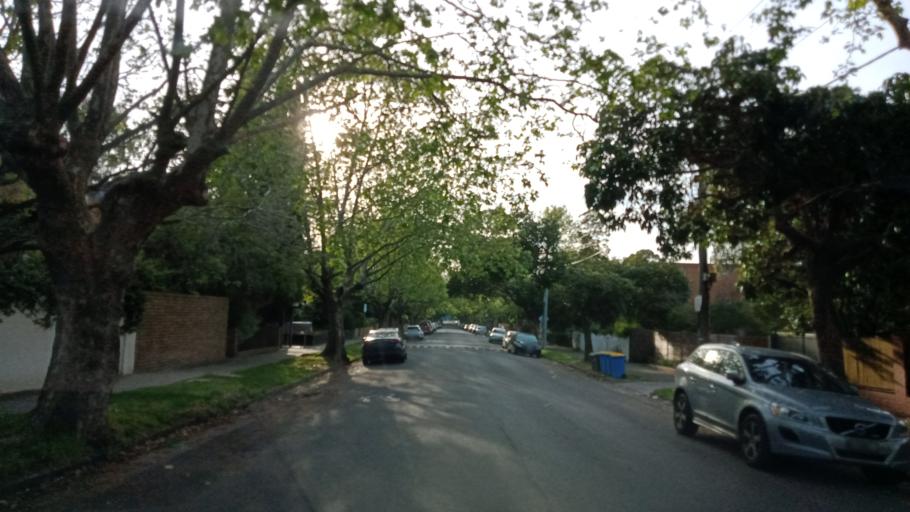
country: AU
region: Victoria
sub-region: Boroondara
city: Hawthorn East
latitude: -37.8253
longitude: 145.0459
